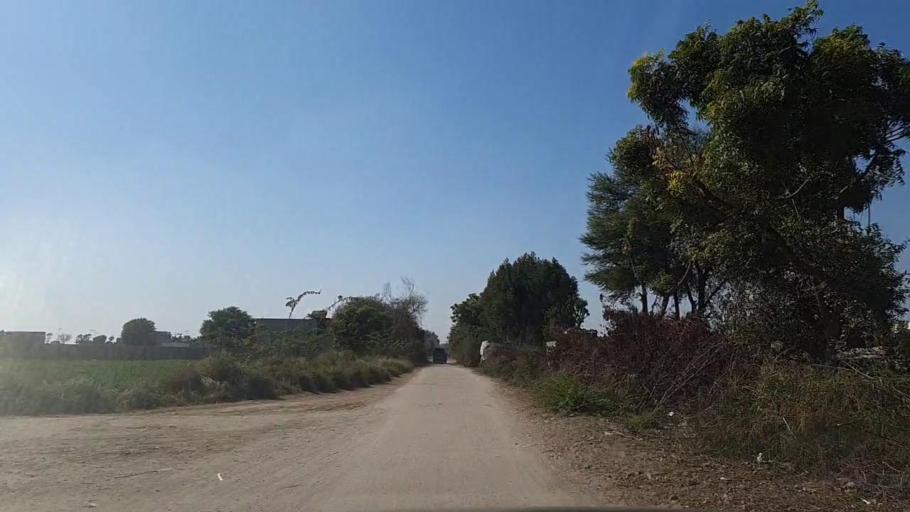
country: PK
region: Sindh
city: Nawabshah
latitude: 26.2446
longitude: 68.4358
